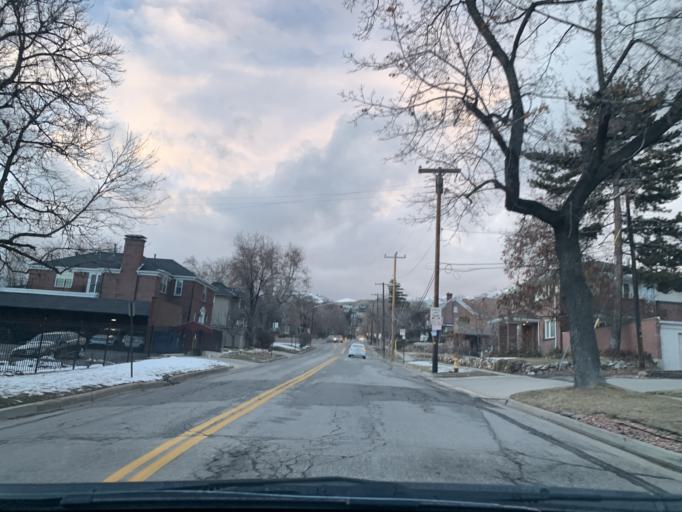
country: US
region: Utah
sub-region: Salt Lake County
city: Salt Lake City
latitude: 40.7695
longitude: -111.8523
